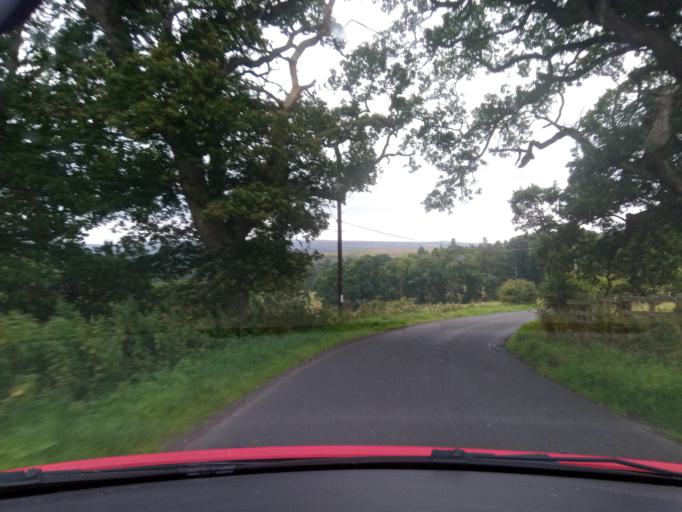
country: GB
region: England
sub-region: Northumberland
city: Otterburn
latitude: 55.3038
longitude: -2.0543
